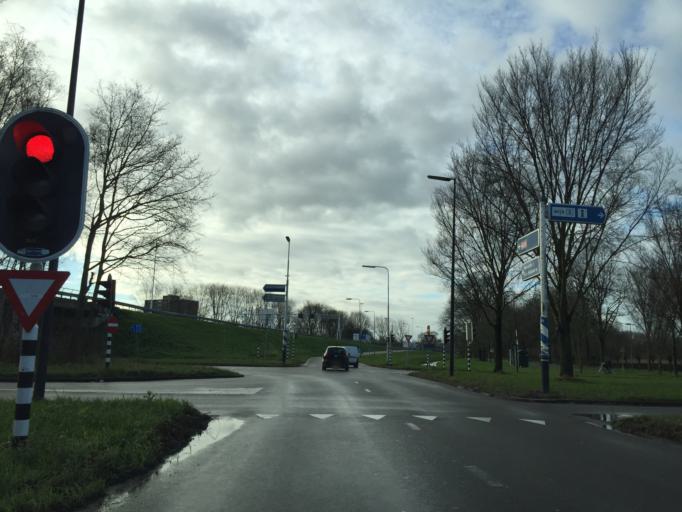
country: NL
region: South Holland
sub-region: Gemeente Vlaardingen
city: Vlaardingen
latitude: 51.9186
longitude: 4.3307
